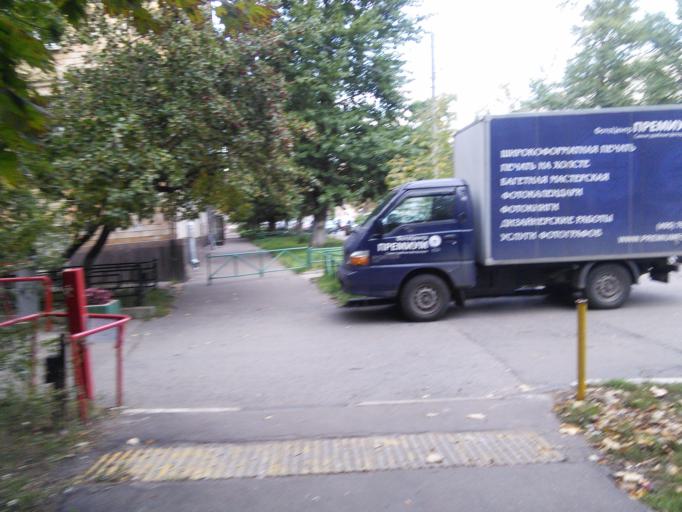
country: RU
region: Moskovskaya
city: Semenovskoye
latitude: 55.6904
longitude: 37.5595
